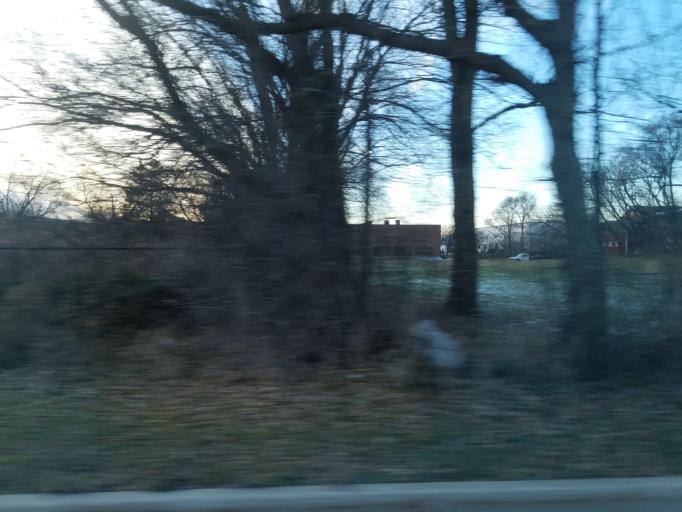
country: US
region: Illinois
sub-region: DuPage County
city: Wood Dale
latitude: 41.9792
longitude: -87.9799
